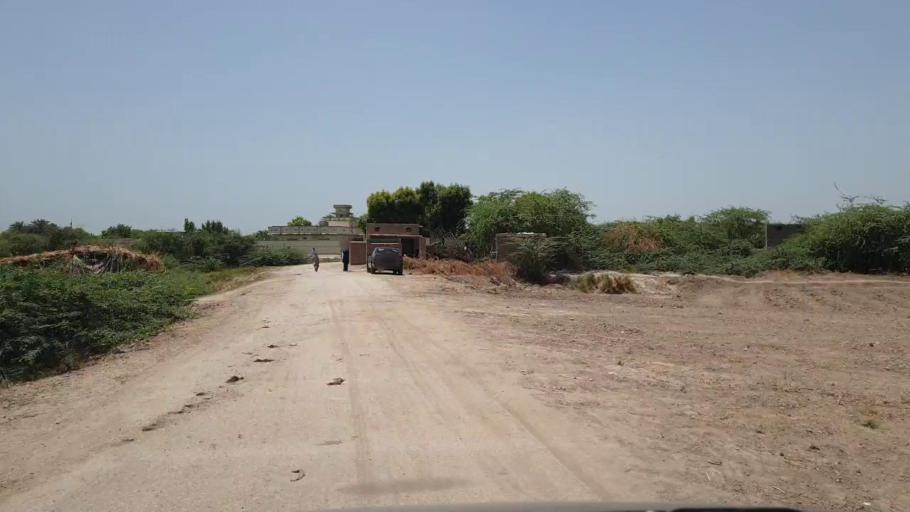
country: PK
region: Sindh
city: Sakrand
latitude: 26.1089
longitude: 68.3900
